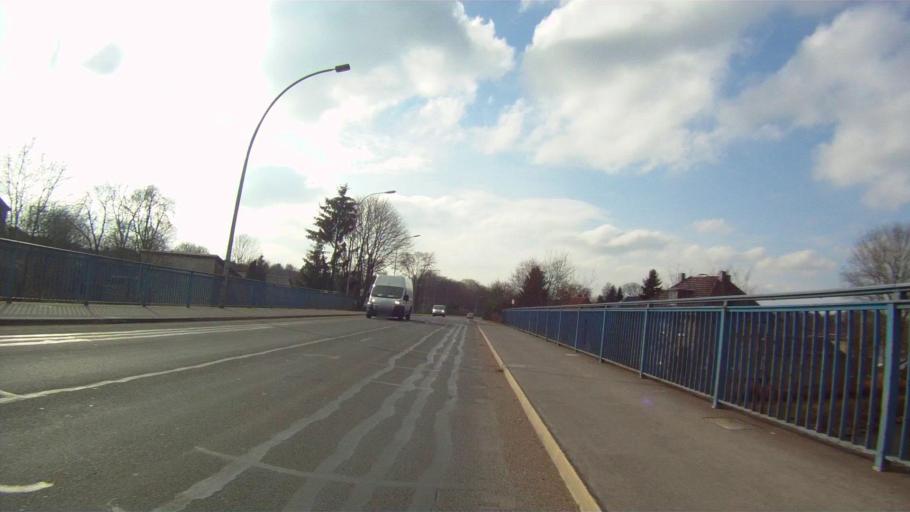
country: DE
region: Berlin
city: Schmockwitz
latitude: 52.3723
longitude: 13.7074
